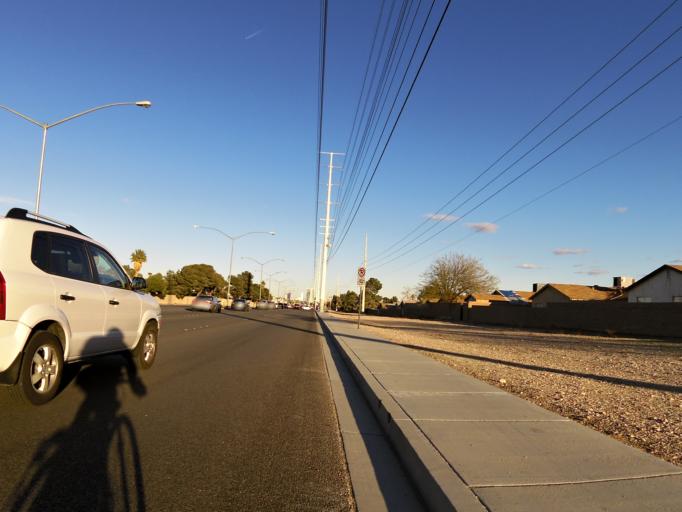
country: US
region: Nevada
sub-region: Clark County
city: Spring Valley
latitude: 36.1144
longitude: -115.2477
